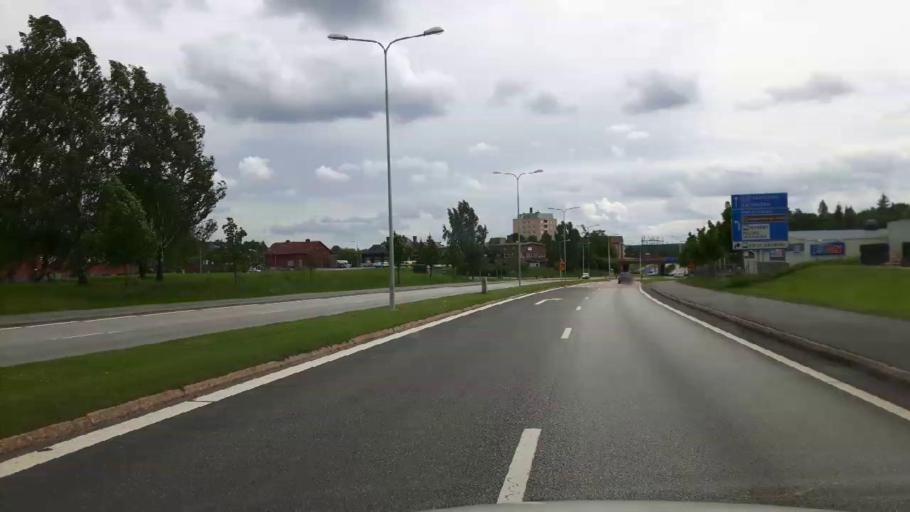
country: SE
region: Vaestmanland
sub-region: Fagersta Kommun
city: Fagersta
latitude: 59.9931
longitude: 15.8109
